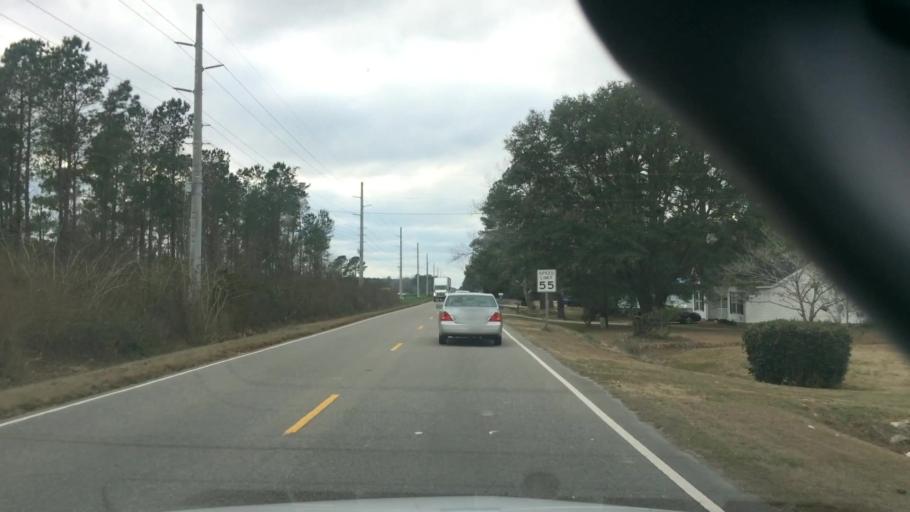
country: US
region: North Carolina
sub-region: Brunswick County
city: Carolina Shores
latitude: 33.9362
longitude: -78.5724
